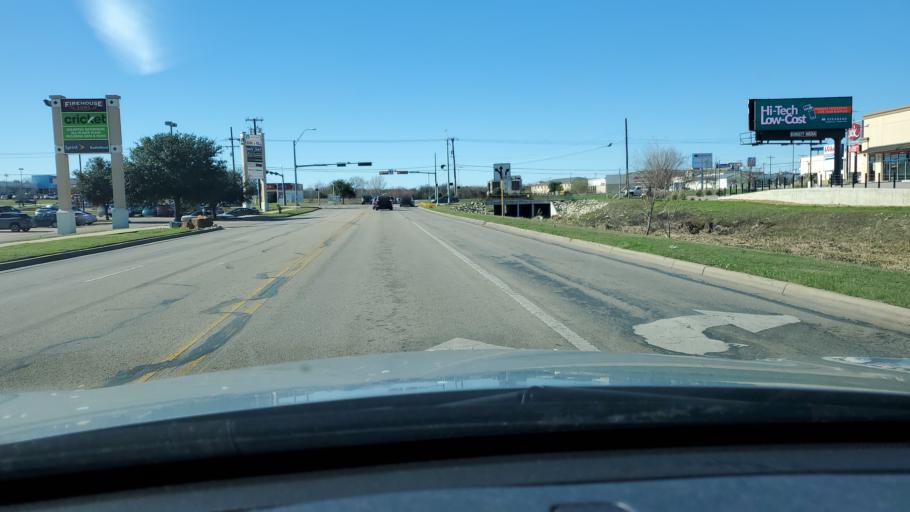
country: US
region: Texas
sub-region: Bell County
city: Killeen
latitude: 31.0922
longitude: -97.7320
